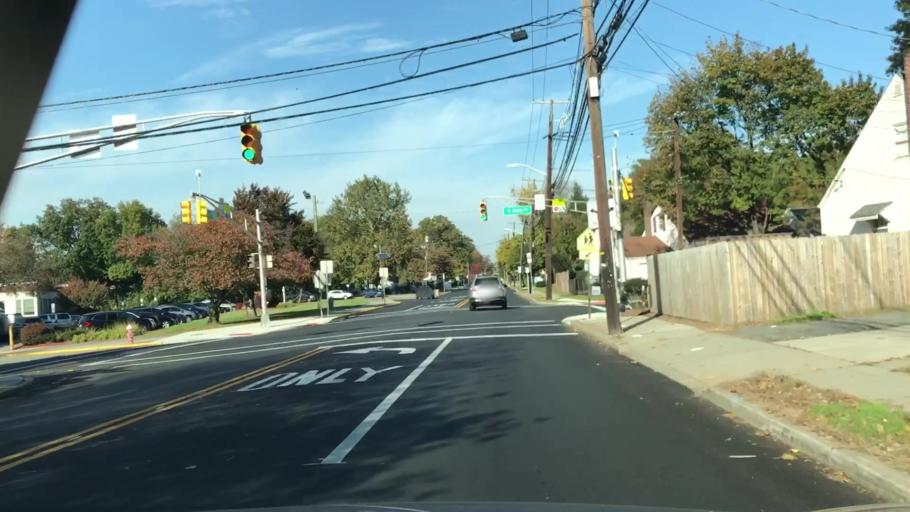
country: US
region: New Jersey
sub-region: Bergen County
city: Bergenfield
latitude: 40.9239
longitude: -74.0063
